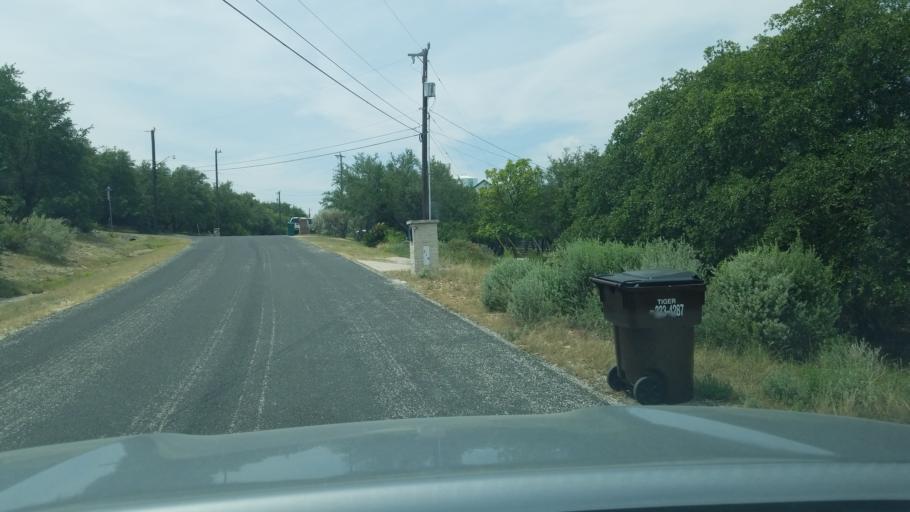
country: US
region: Texas
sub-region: Bexar County
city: Timberwood Park
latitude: 29.6870
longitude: -98.5078
